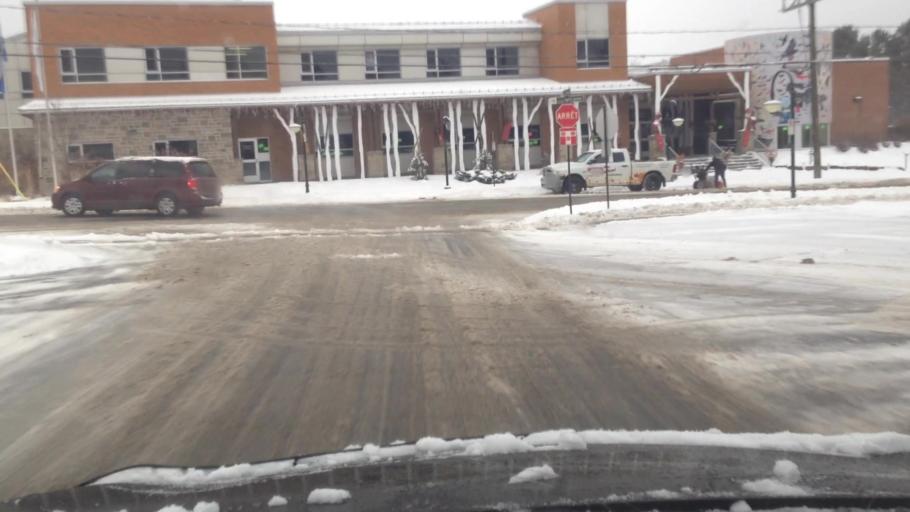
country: CA
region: Quebec
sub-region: Laurentides
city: Mont-Tremblant
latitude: 46.1187
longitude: -74.6002
